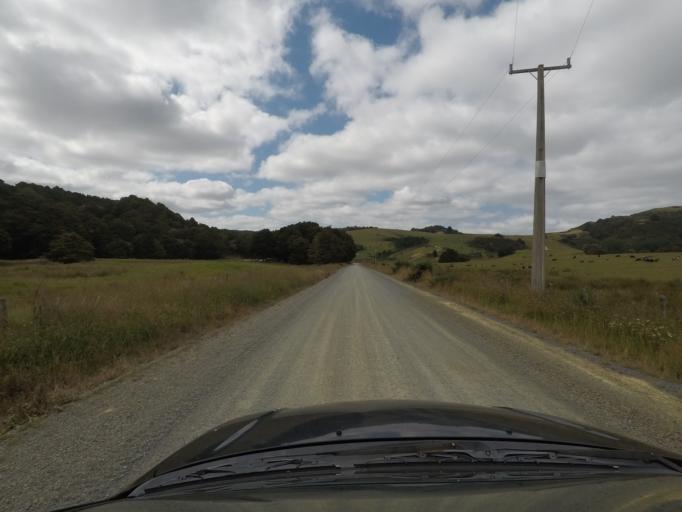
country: NZ
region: Northland
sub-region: Whangarei
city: Ruakaka
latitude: -35.9325
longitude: 174.3470
